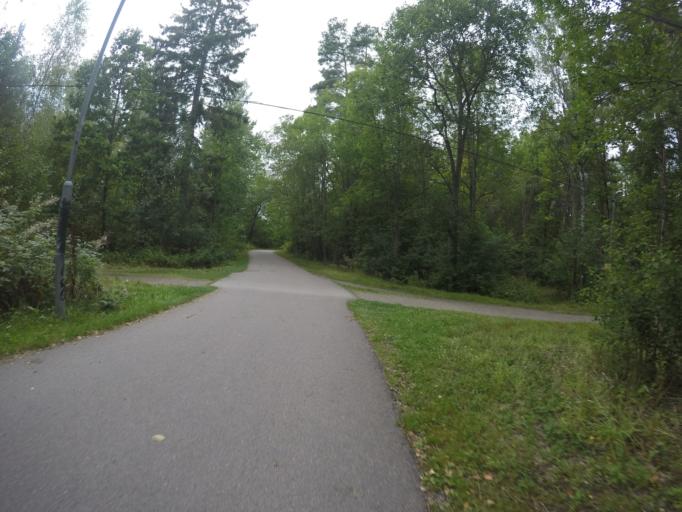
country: SE
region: Vaestmanland
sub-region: Vasteras
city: Vasteras
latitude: 59.6462
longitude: 16.5139
